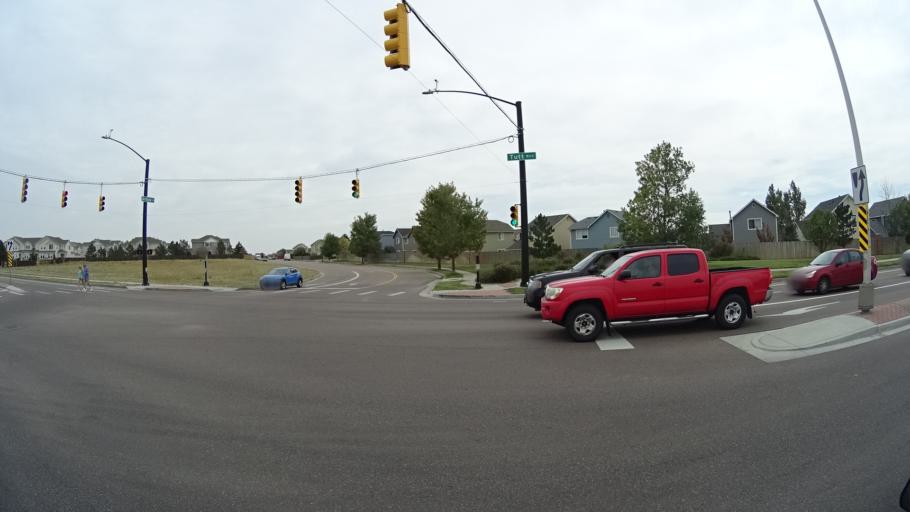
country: US
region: Colorado
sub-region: El Paso County
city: Cimarron Hills
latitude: 38.9241
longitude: -104.7160
